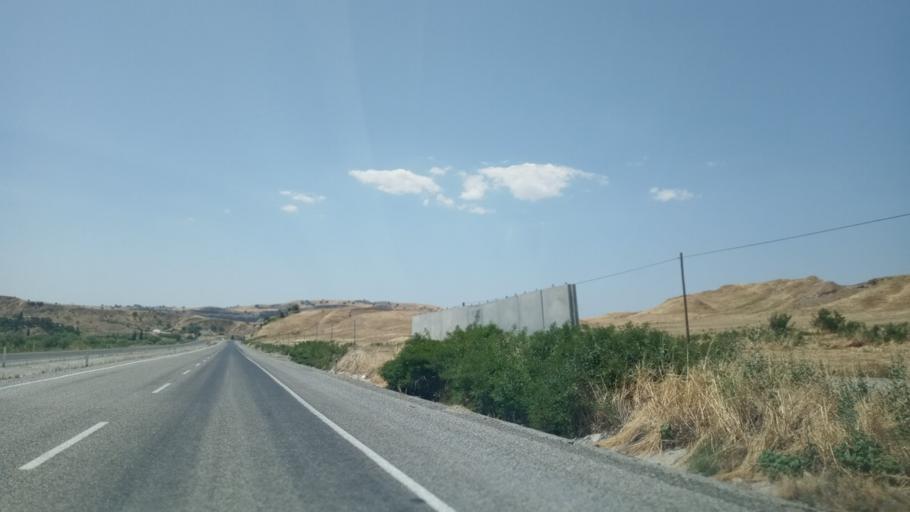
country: TR
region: Batman
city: Kozluk
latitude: 38.1553
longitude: 41.4121
